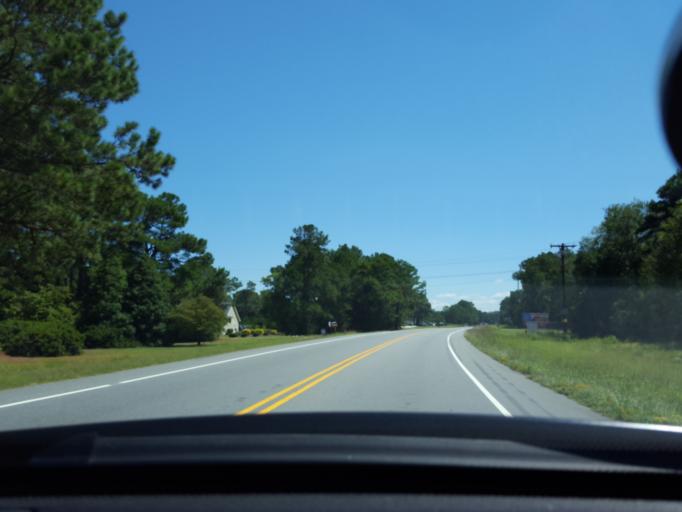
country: US
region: North Carolina
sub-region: Bladen County
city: Elizabethtown
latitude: 34.6501
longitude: -78.5397
